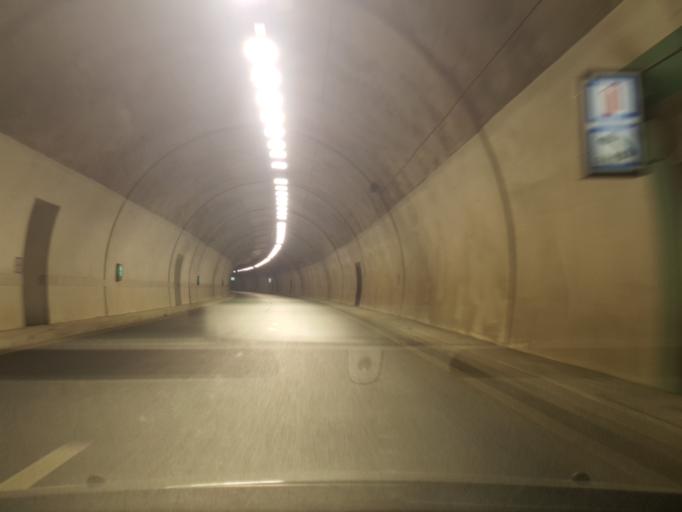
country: RS
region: Central Serbia
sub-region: Pirotski Okrug
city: Dimitrovgrad
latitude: 43.0238
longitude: 22.7931
